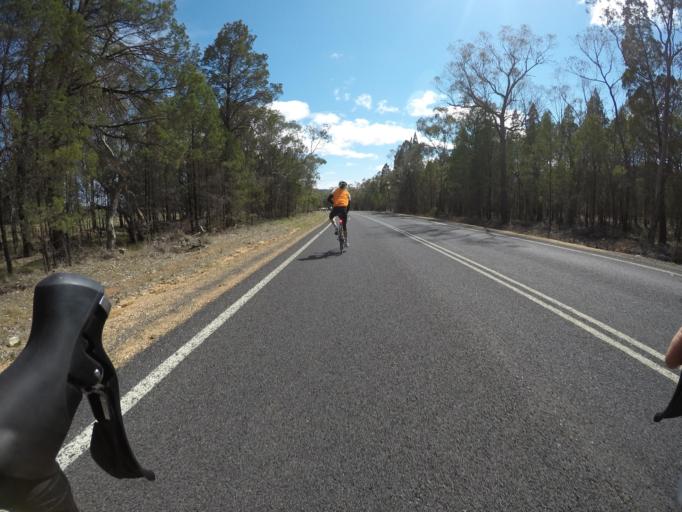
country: AU
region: New South Wales
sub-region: Parkes
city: Peak Hill
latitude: -32.6776
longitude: 148.5598
